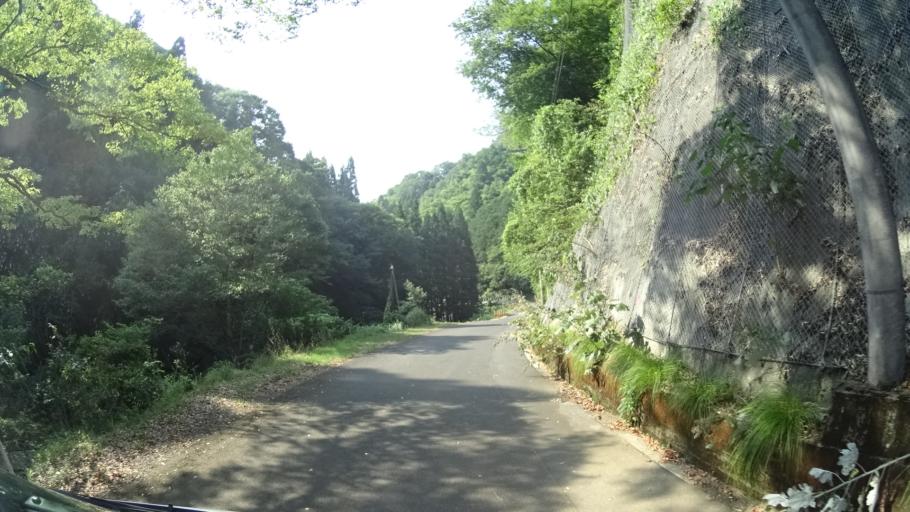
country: JP
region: Kyoto
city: Maizuru
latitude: 35.4077
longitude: 135.2344
